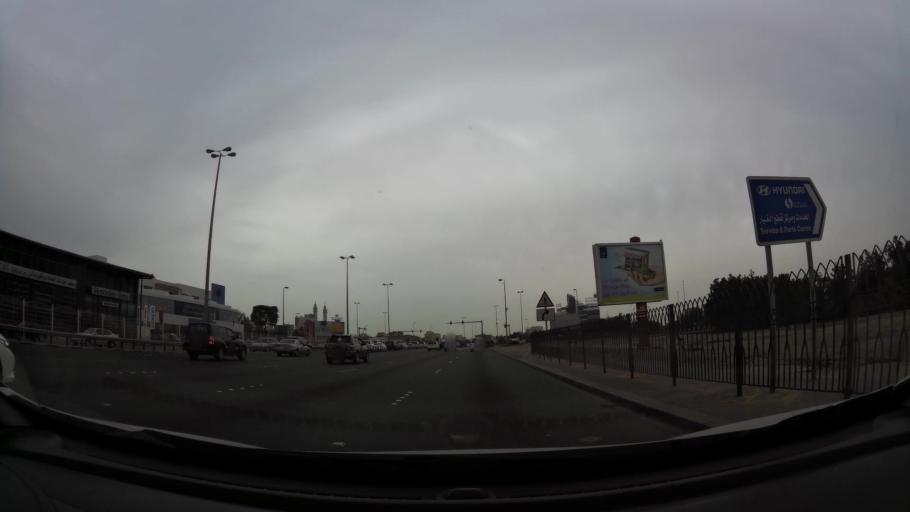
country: BH
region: Northern
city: Madinat `Isa
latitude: 26.1880
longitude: 50.5361
